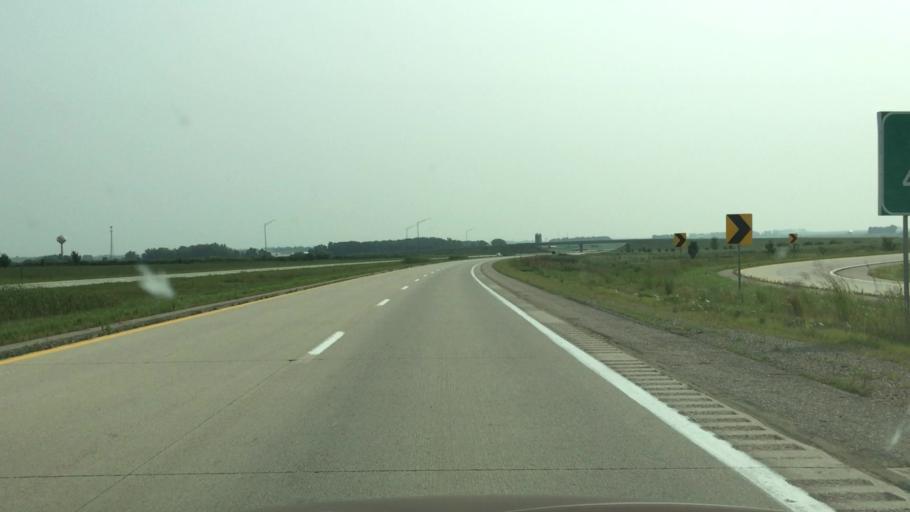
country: US
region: Iowa
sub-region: Osceola County
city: Sibley
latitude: 43.3823
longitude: -95.7499
